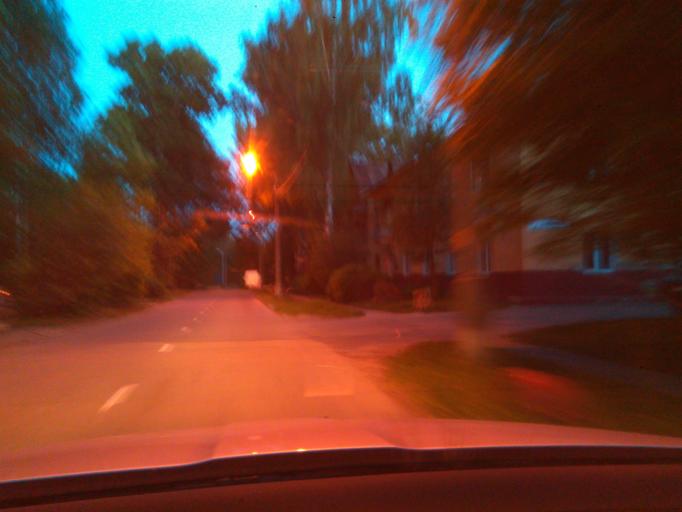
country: RU
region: Moskovskaya
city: Dolgoprudnyy
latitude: 55.9587
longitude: 37.5033
